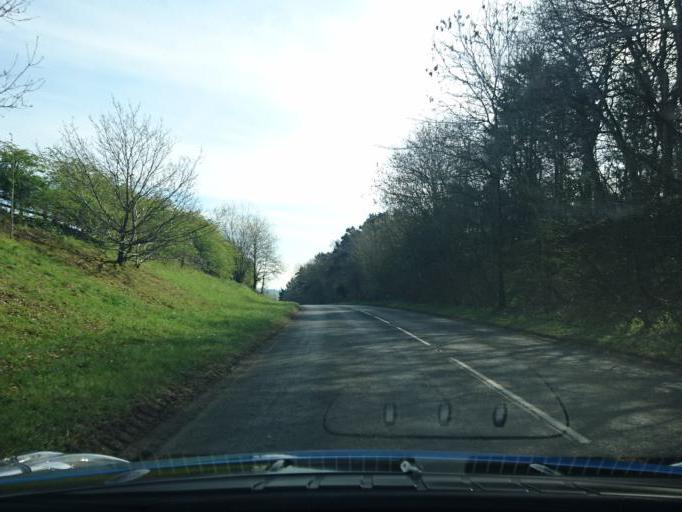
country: GB
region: England
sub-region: Herefordshire
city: Donnington
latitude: 52.0042
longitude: -2.4001
